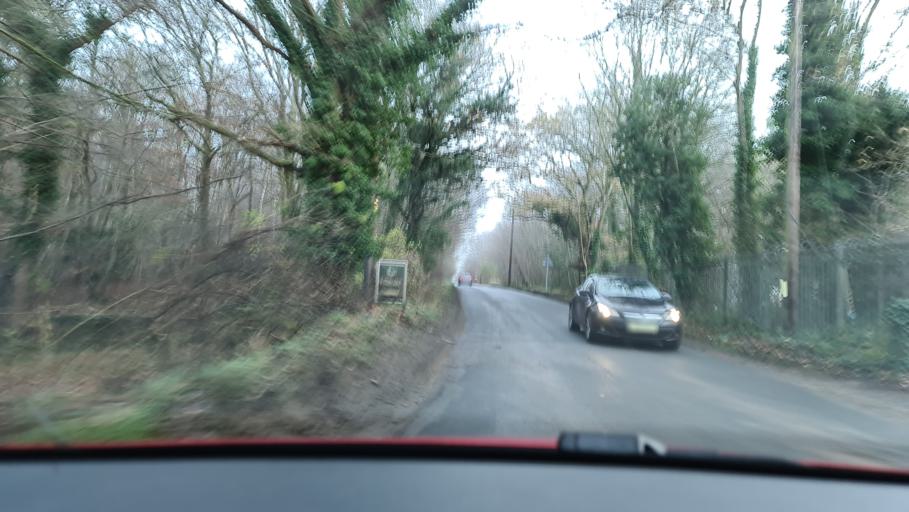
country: GB
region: England
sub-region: Buckinghamshire
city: Seer Green
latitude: 51.6005
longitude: -0.6062
